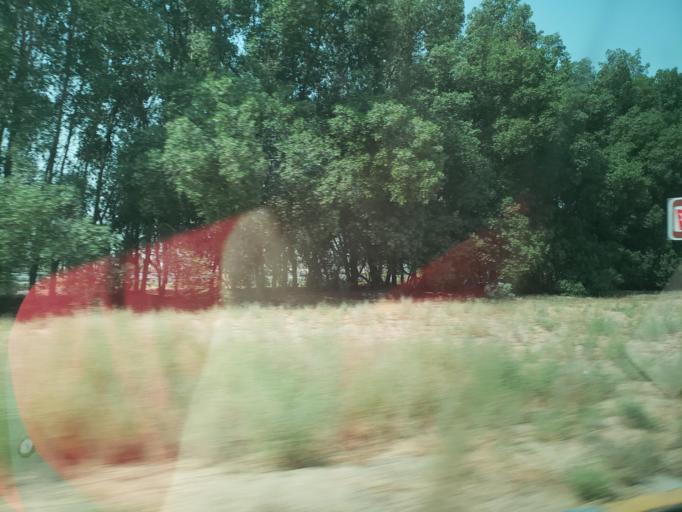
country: AE
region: Ash Shariqah
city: Sharjah
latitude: 25.3218
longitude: 55.5041
